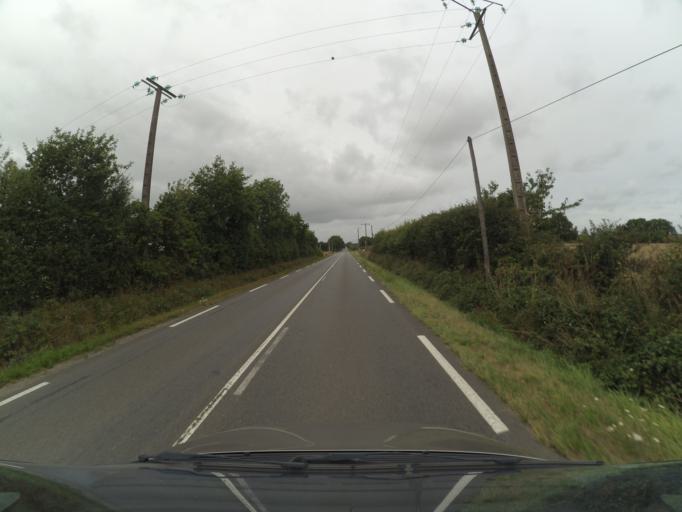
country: FR
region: Pays de la Loire
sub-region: Departement de la Loire-Atlantique
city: Touvois
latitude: 46.8828
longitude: -1.6637
